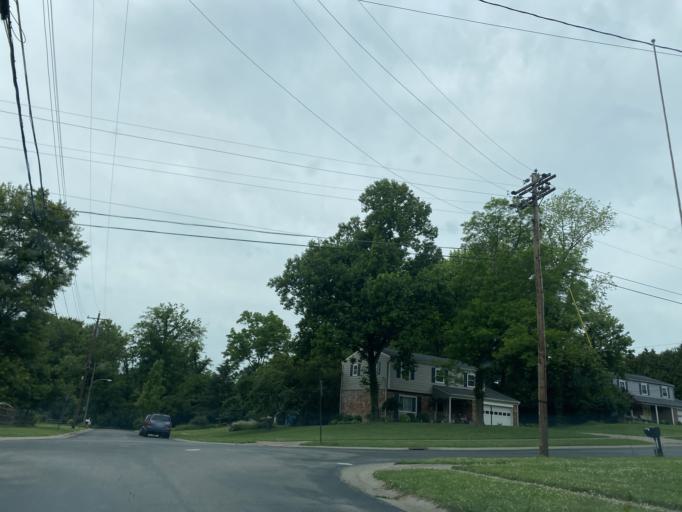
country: US
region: Ohio
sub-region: Hamilton County
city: Salem Heights
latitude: 39.0845
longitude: -84.4031
